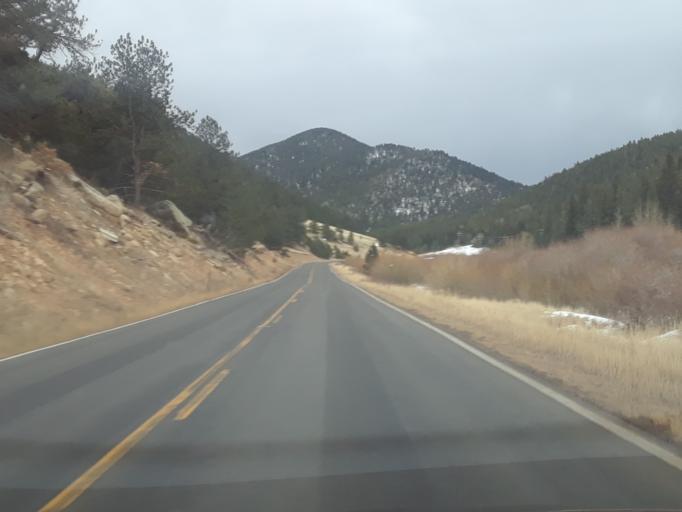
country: US
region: Colorado
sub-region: Boulder County
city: Coal Creek
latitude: 39.8325
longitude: -105.4264
